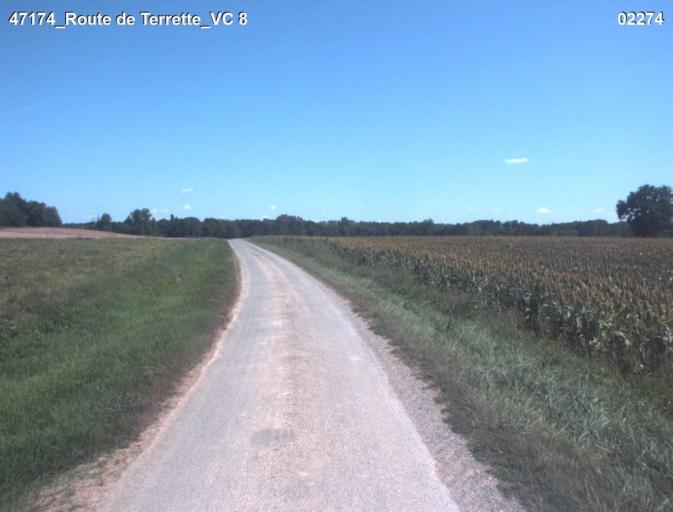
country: FR
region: Aquitaine
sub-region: Departement du Lot-et-Garonne
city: Laplume
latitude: 44.0423
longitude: 0.4446
